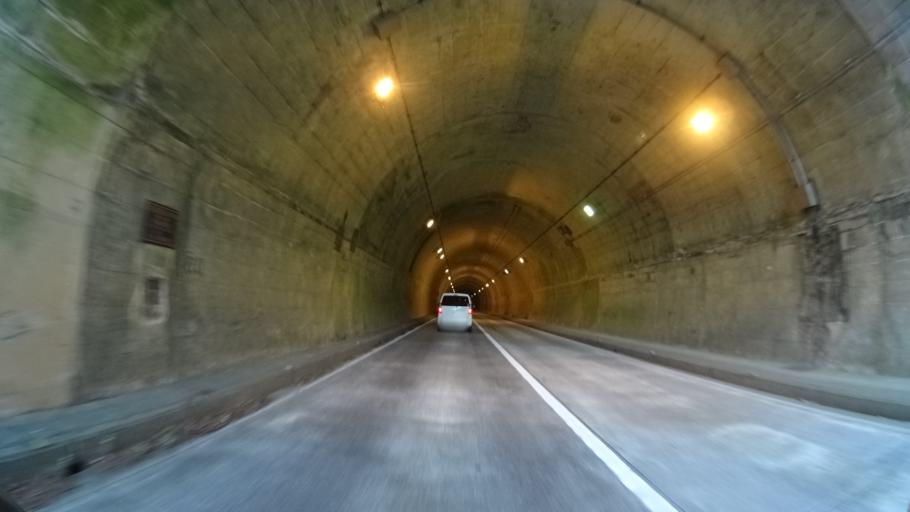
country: JP
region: Ehime
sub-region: Nishiuwa-gun
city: Ikata-cho
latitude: 33.4344
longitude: 132.2310
